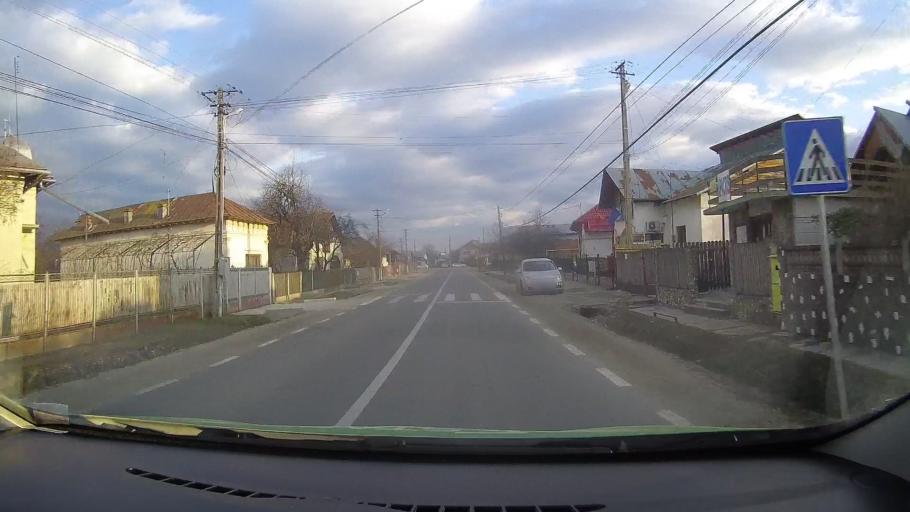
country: RO
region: Dambovita
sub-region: Comuna I. L. Caragiale
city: Ghirdoveni
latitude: 44.9397
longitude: 25.6727
